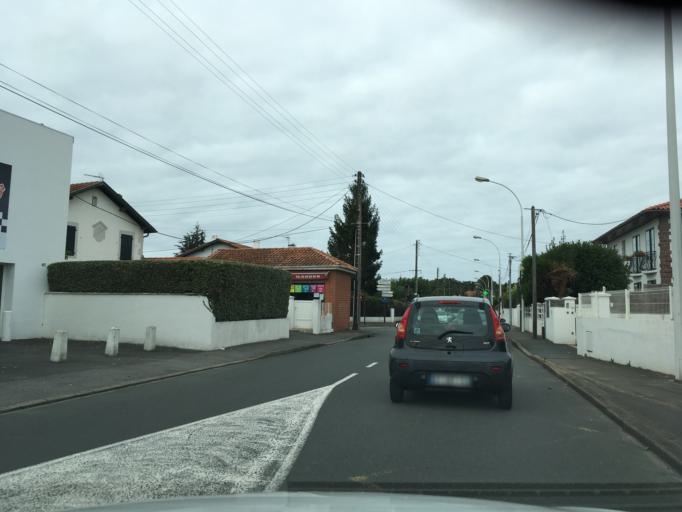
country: FR
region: Aquitaine
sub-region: Departement des Pyrenees-Atlantiques
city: Biarritz
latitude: 43.4729
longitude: -1.5407
